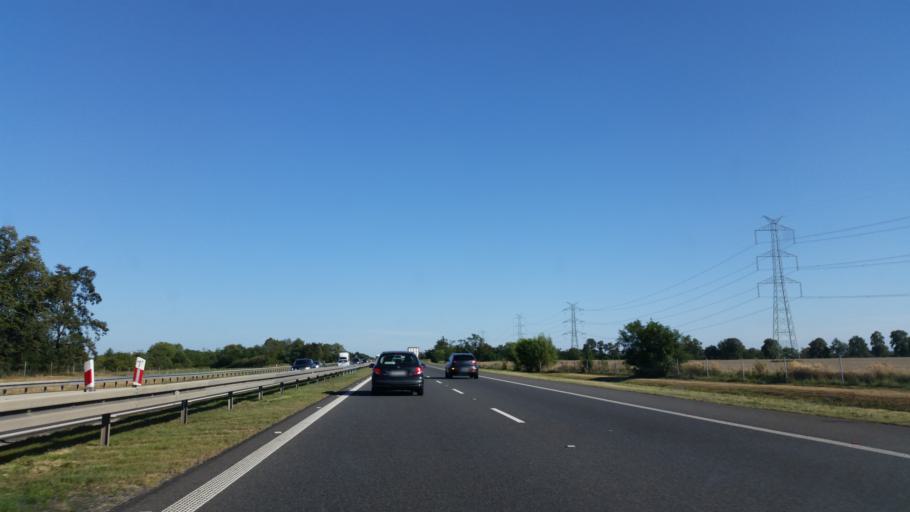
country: PL
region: Lower Silesian Voivodeship
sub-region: Powiat strzelinski
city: Wiazow
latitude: 50.8305
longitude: 17.2897
